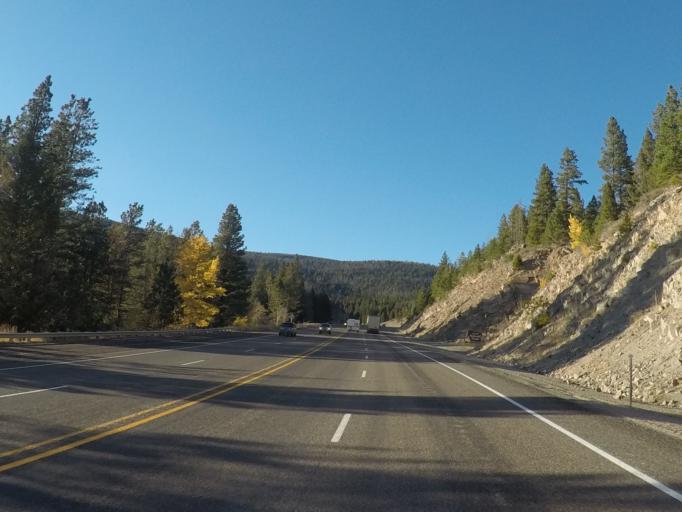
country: US
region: Montana
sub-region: Lewis and Clark County
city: Helena West Side
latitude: 46.5839
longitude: -112.2616
